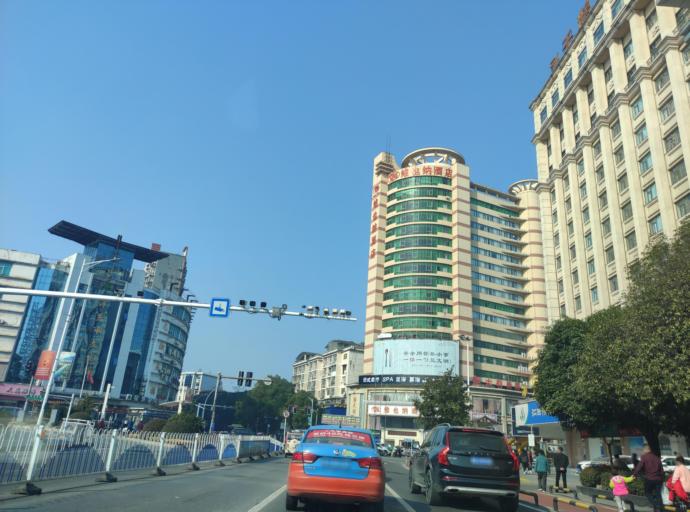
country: CN
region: Jiangxi Sheng
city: Pingxiang
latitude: 27.6336
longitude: 113.8437
